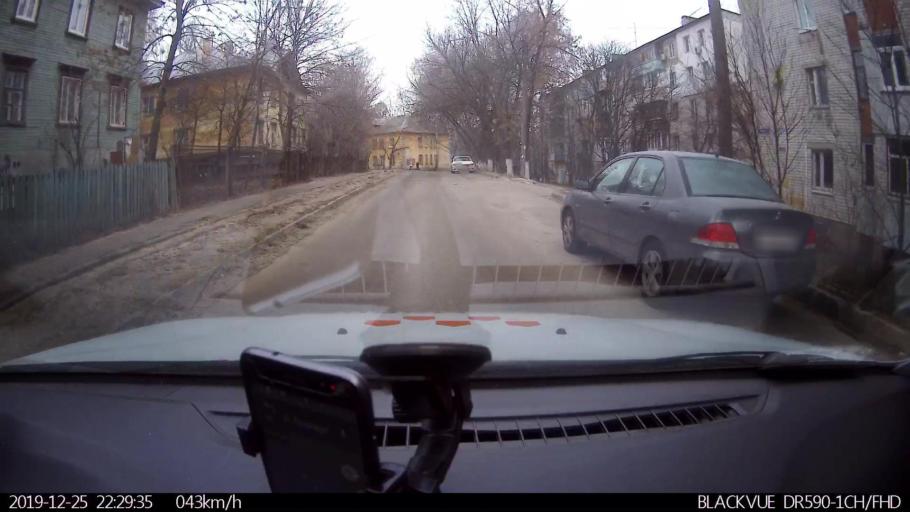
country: RU
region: Nizjnij Novgorod
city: Nizhniy Novgorod
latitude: 56.2690
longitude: 43.9849
